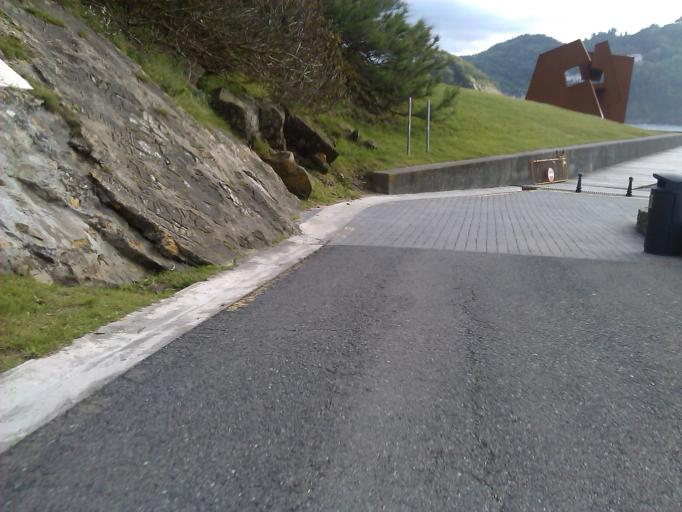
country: ES
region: Basque Country
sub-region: Provincia de Guipuzcoa
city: San Sebastian
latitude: 43.3247
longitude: -1.9930
